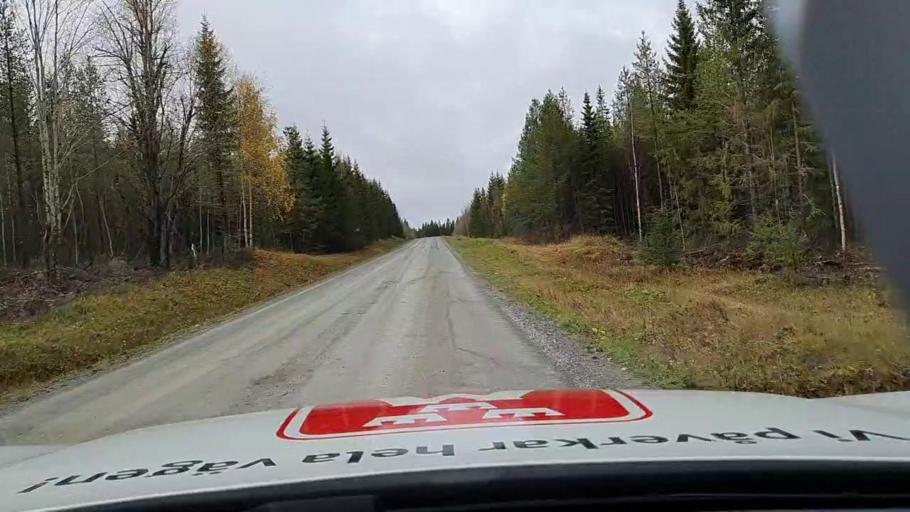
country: SE
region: Jaemtland
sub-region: Bergs Kommun
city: Hoverberg
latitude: 62.9991
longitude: 14.1471
